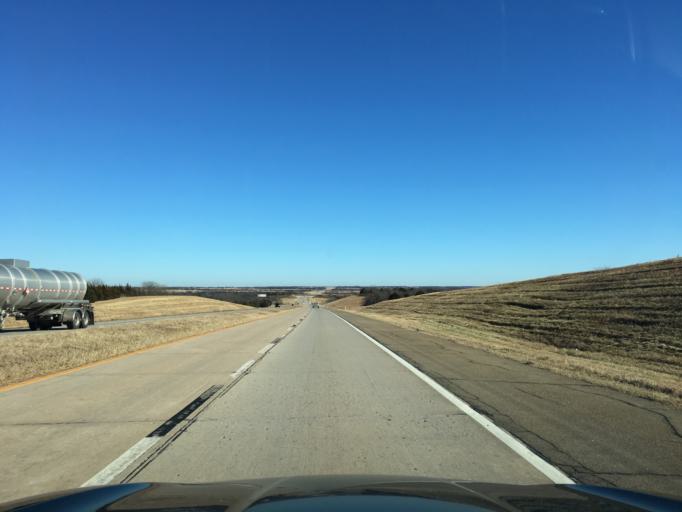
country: US
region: Oklahoma
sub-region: Payne County
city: Yale
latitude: 36.2241
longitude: -96.7275
